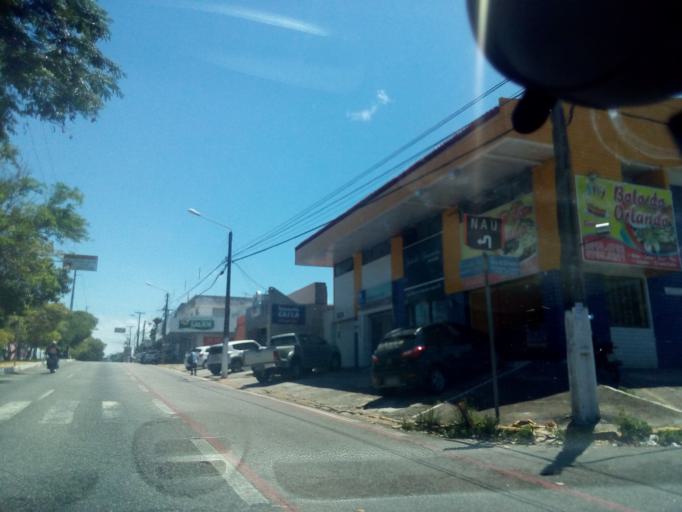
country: BR
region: Rio Grande do Norte
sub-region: Natal
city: Natal
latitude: -5.8344
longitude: -35.2185
